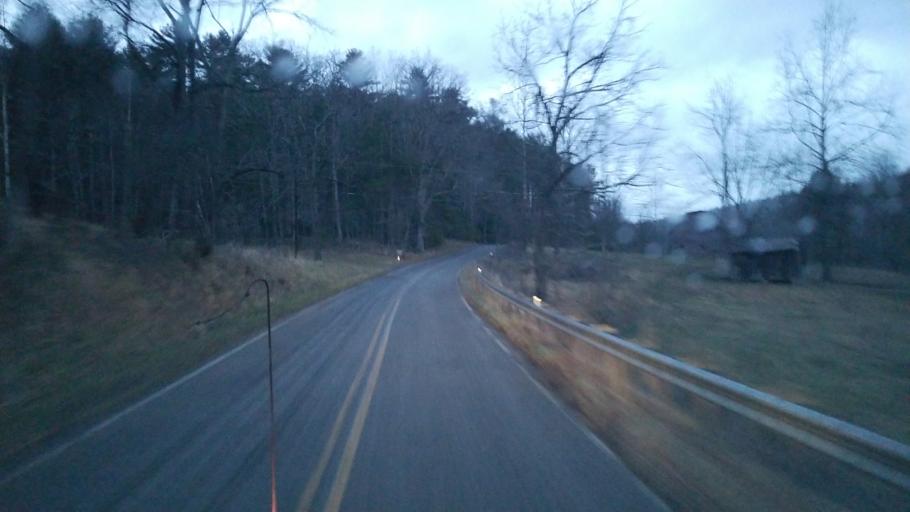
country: US
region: Virginia
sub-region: Pulaski County
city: Pulaski
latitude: 37.1202
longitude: -80.8723
